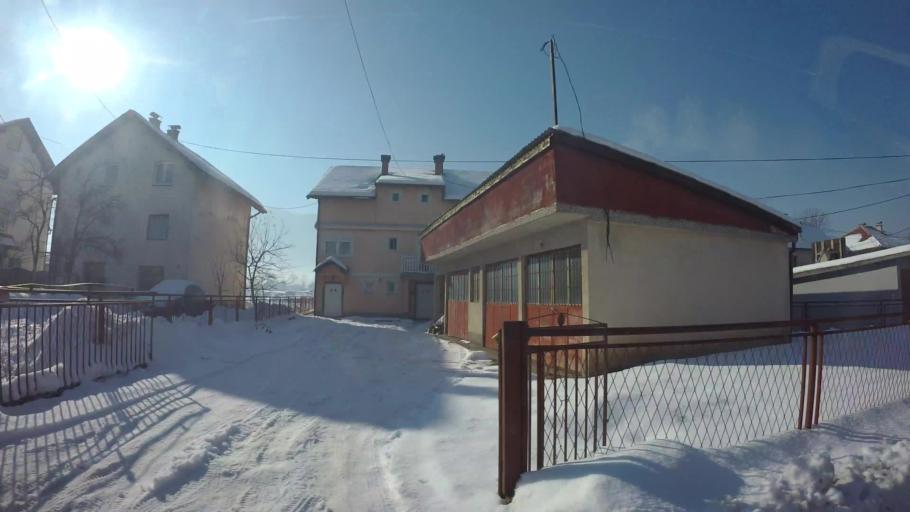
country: BA
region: Federation of Bosnia and Herzegovina
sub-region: Kanton Sarajevo
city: Sarajevo
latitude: 43.8139
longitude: 18.3124
